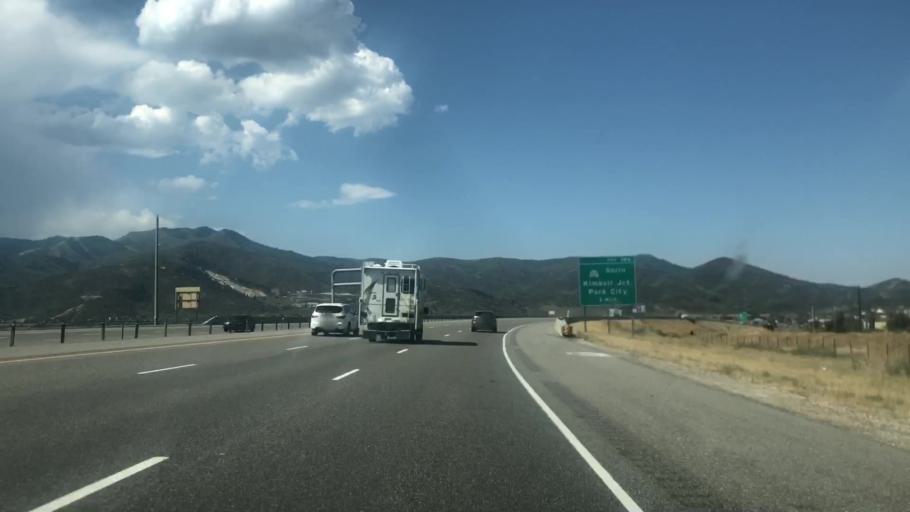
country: US
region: Utah
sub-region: Summit County
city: Snyderville
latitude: 40.7213
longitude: -111.5196
